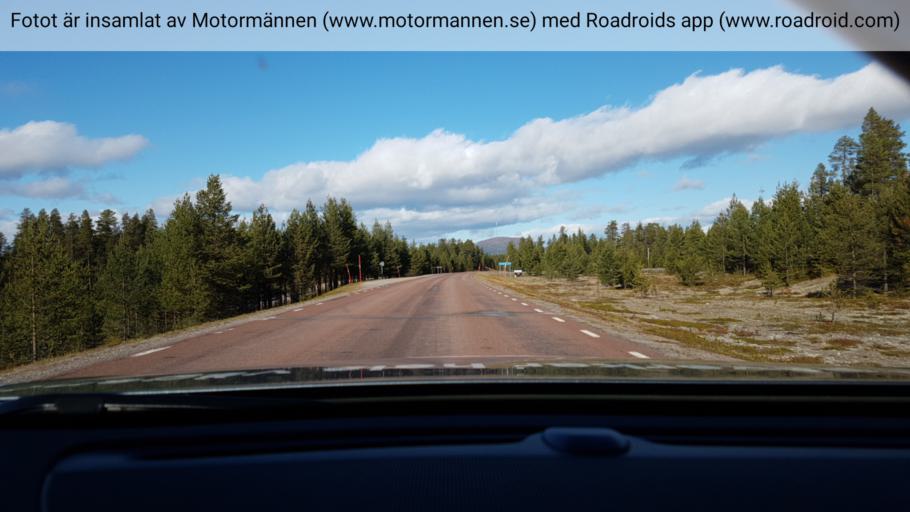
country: SE
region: Norrbotten
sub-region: Arjeplogs Kommun
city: Arjeplog
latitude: 66.0399
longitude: 18.0412
